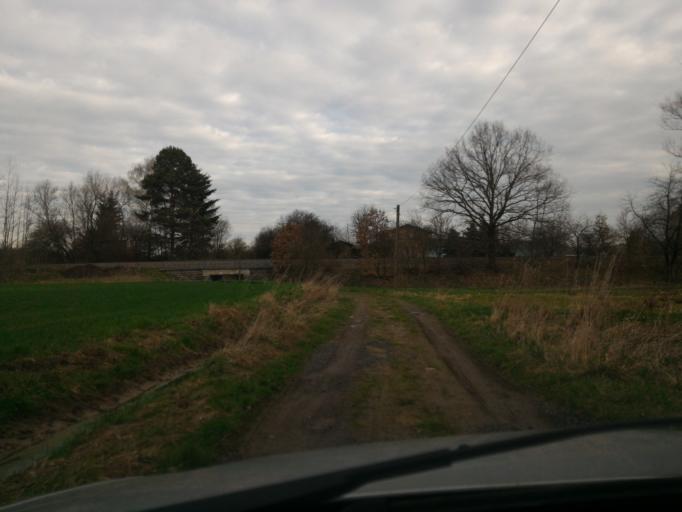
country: DE
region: Saxony
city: Eibau
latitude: 50.9661
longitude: 14.6709
